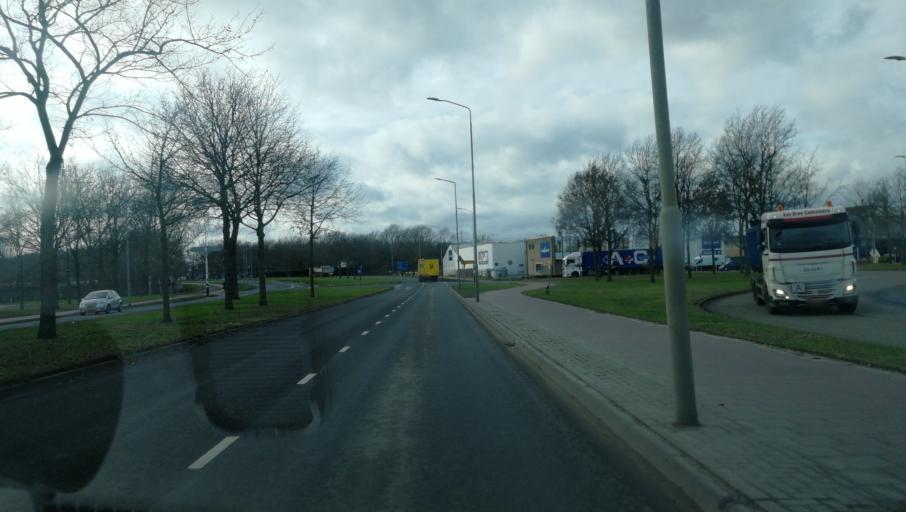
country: NL
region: Limburg
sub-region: Gemeente Venlo
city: Venlo
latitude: 51.3817
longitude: 6.1423
